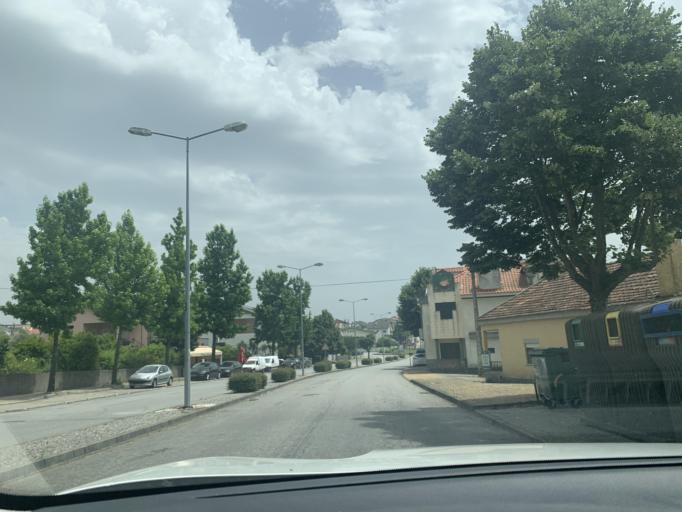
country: PT
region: Viseu
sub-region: Mangualde
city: Mangualde
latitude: 40.5987
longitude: -7.7597
